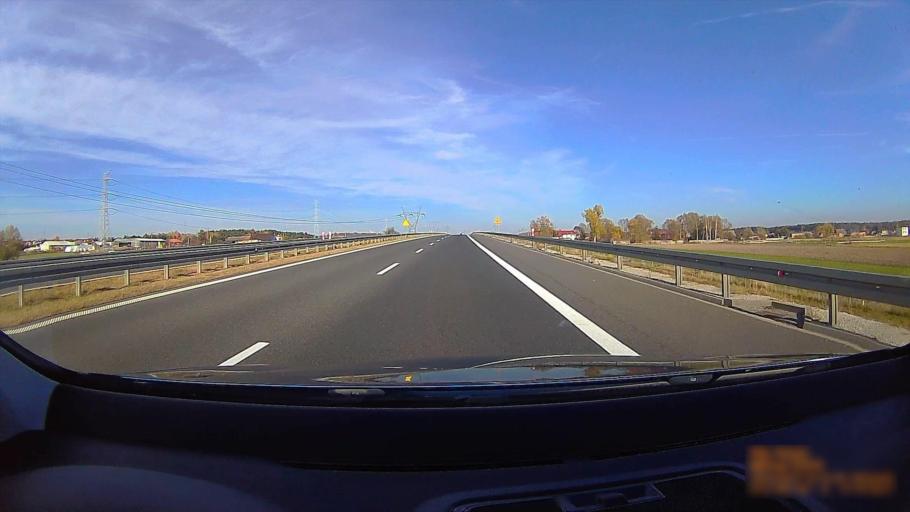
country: PL
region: Greater Poland Voivodeship
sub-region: Powiat ostrowski
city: Przygodzice
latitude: 51.6023
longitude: 17.8530
